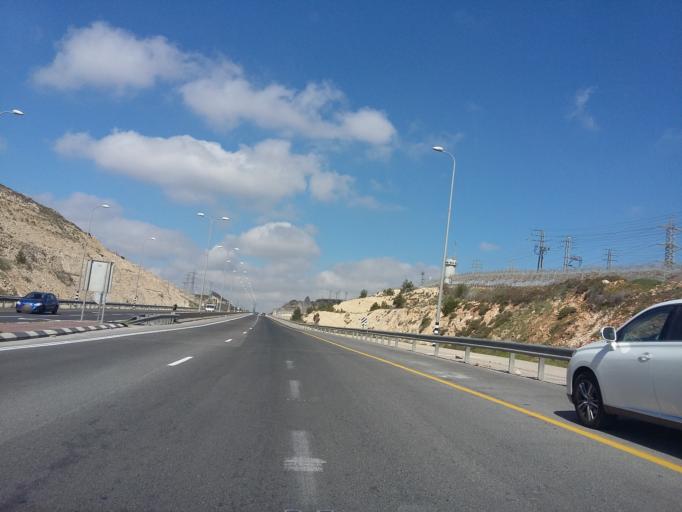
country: PS
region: West Bank
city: Qalandiya
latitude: 31.8583
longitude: 35.2076
